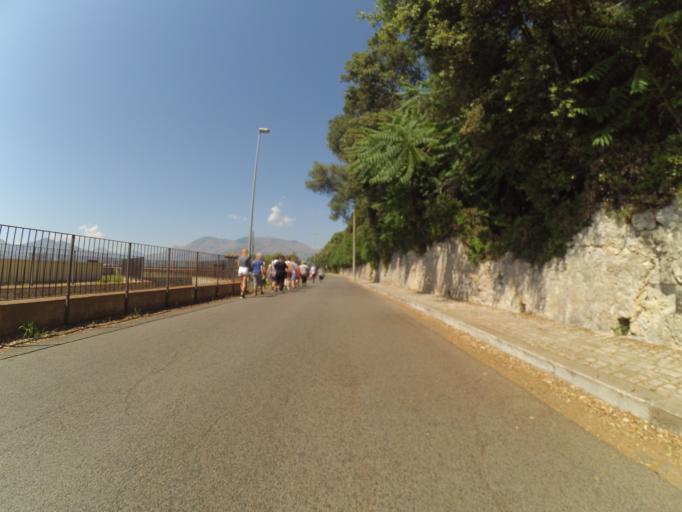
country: IT
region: Latium
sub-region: Provincia di Latina
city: Gaeta
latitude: 41.2081
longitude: 13.5725
